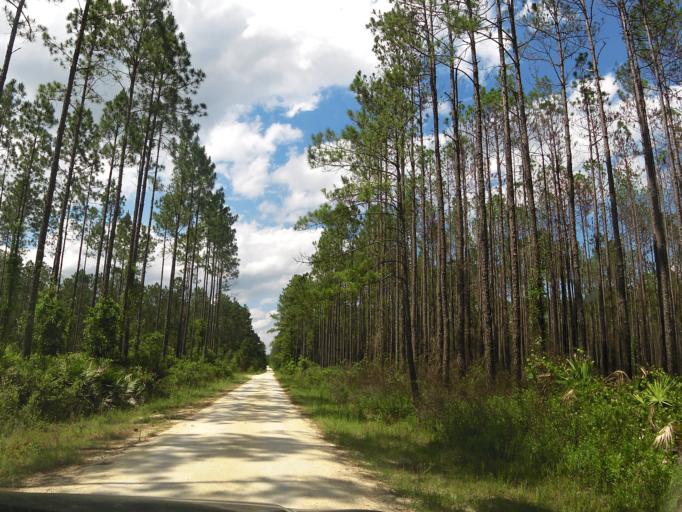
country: US
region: Florida
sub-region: Clay County
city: Asbury Lake
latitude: 29.8799
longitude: -81.8528
